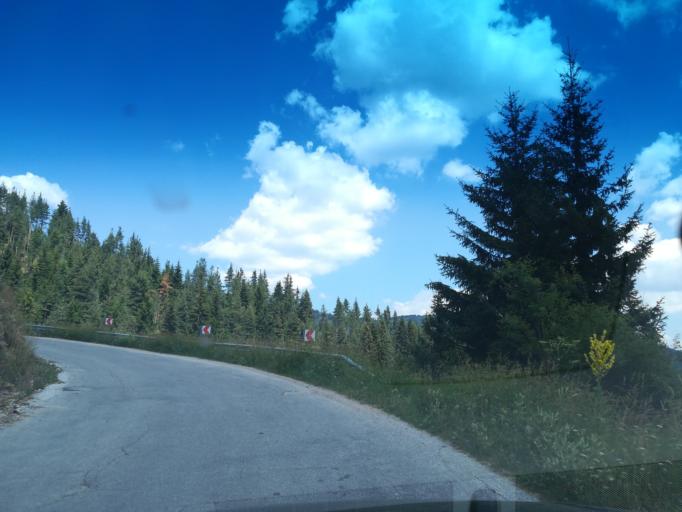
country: BG
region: Smolyan
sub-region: Obshtina Chepelare
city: Chepelare
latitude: 41.6782
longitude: 24.7705
